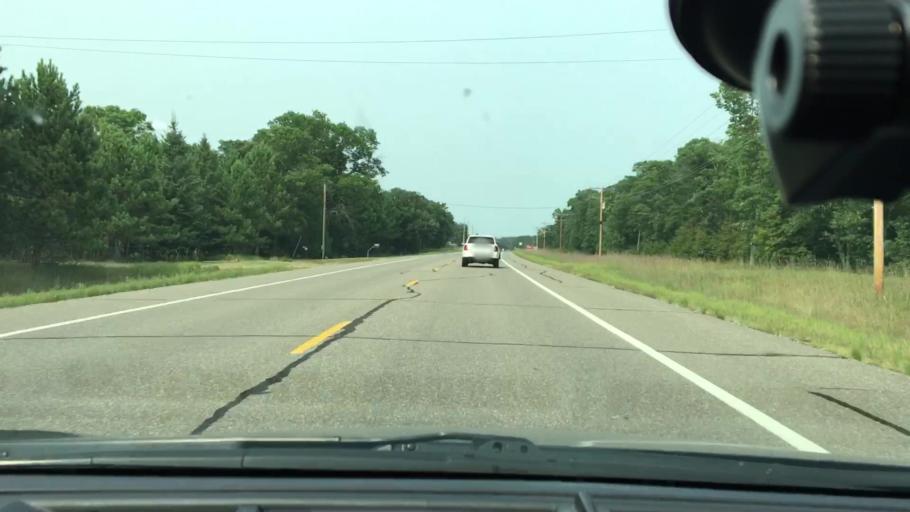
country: US
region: Minnesota
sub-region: Crow Wing County
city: Cross Lake
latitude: 46.6102
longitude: -94.1317
